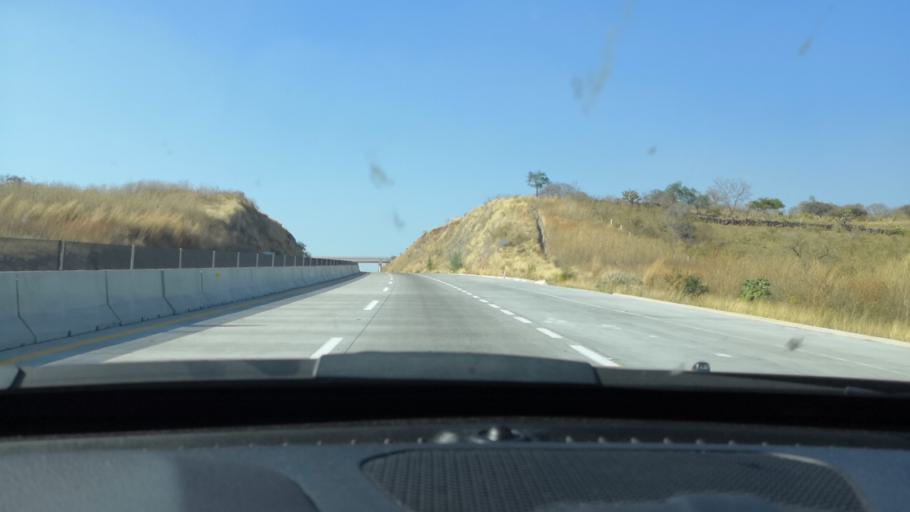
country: MX
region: Jalisco
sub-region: Zapotlanejo
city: La Mezquitera
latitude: 20.5892
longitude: -103.0991
